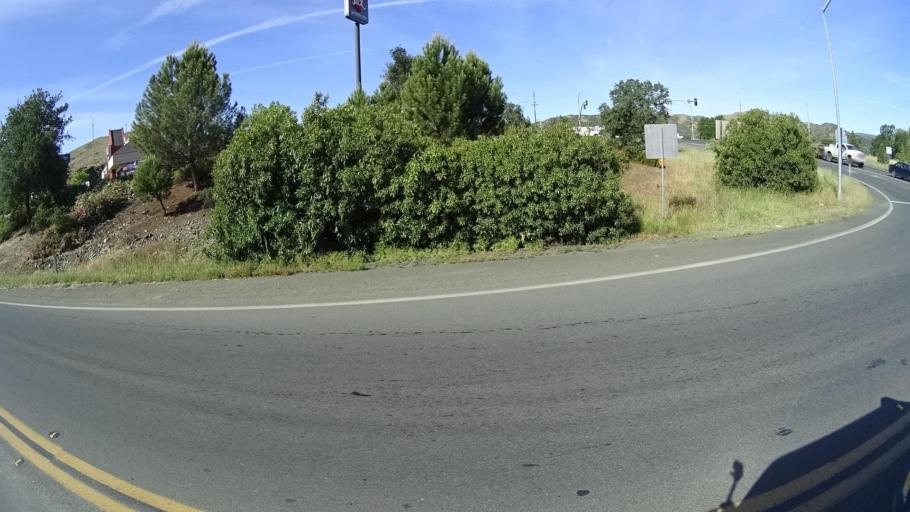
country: US
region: California
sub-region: Lake County
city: Lakeport
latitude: 39.0170
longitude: -122.9119
